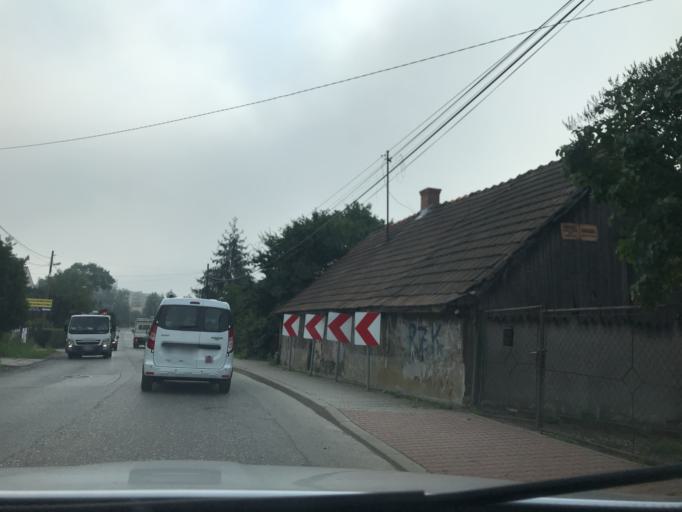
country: PL
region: Lesser Poland Voivodeship
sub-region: Powiat krakowski
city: Ochojno
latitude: 50.0025
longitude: 20.0013
